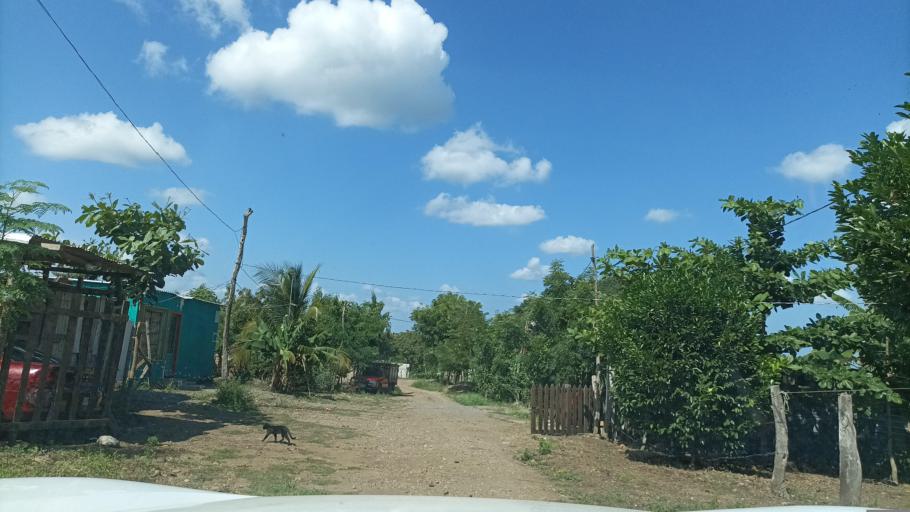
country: MX
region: Veracruz
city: Manlio Fabio Altamirano
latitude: 19.0872
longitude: -96.3427
